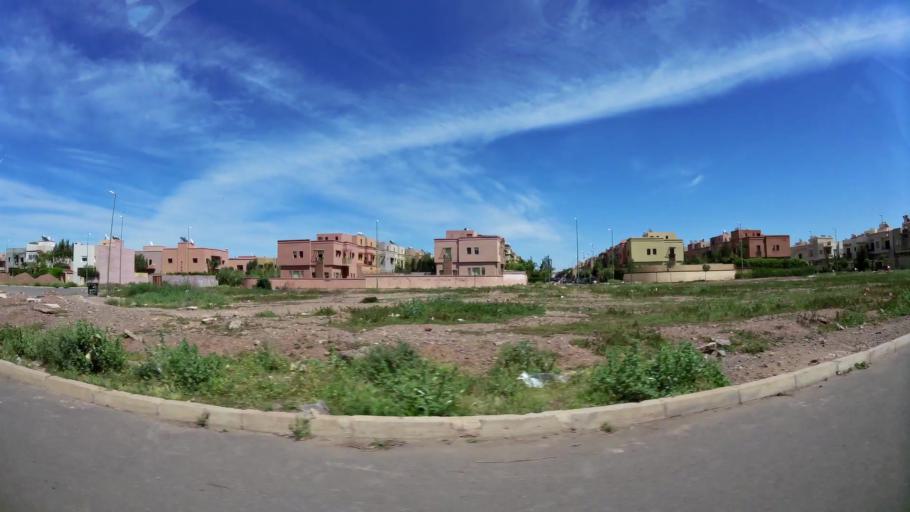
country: MA
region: Marrakech-Tensift-Al Haouz
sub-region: Marrakech
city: Marrakesh
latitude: 31.6536
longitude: -8.0812
